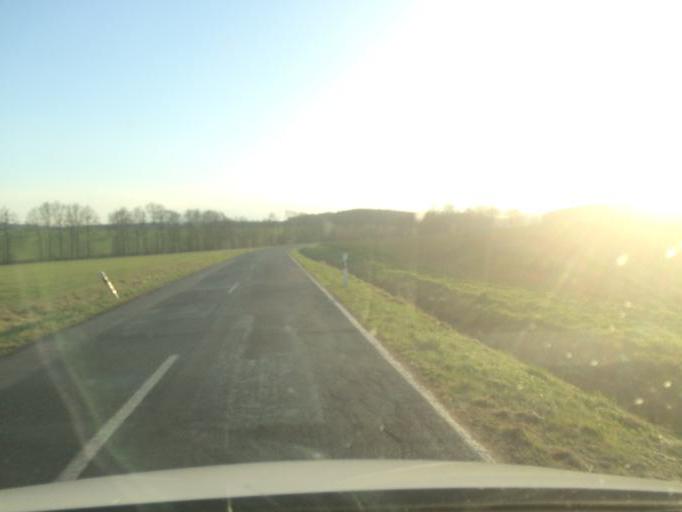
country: DE
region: Thuringia
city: Grossbodungen
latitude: 51.5315
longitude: 10.4935
